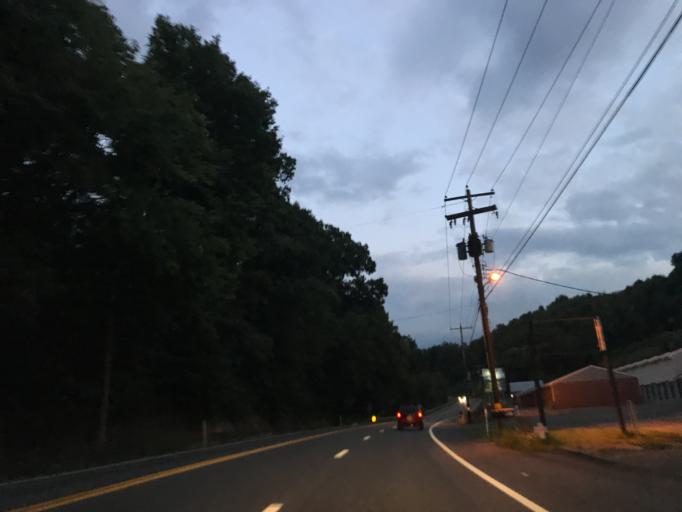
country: US
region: West Virginia
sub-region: Hancock County
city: Chester
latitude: 40.6037
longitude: -80.5473
